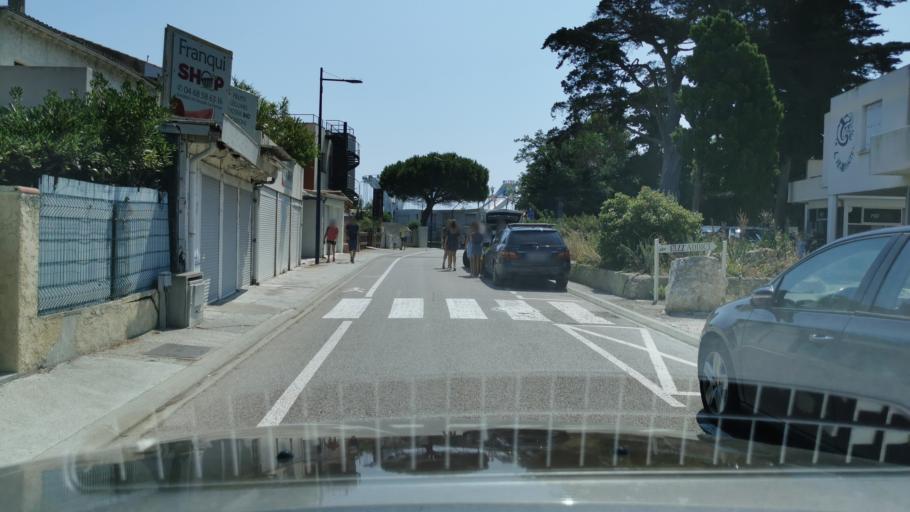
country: FR
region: Languedoc-Roussillon
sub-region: Departement de l'Aude
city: Leucate
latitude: 42.9332
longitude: 3.0348
